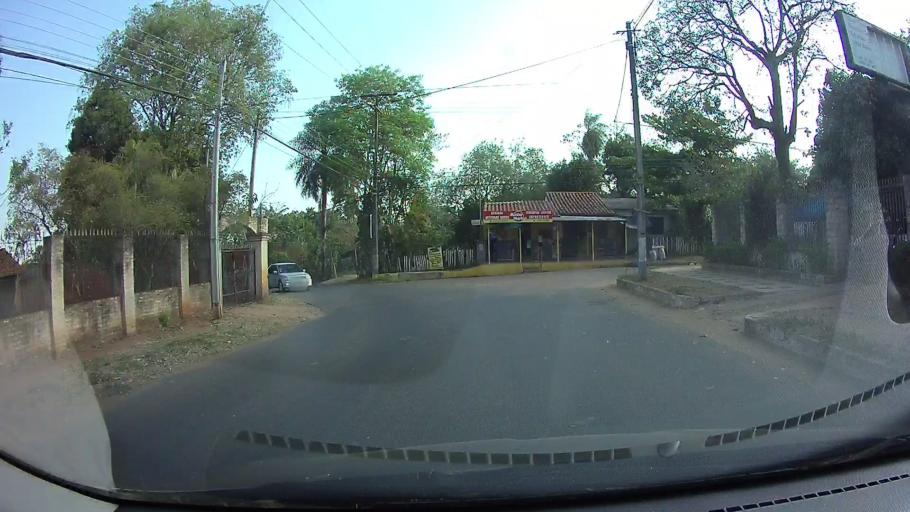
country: PY
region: Central
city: Limpio
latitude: -25.2047
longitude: -57.5069
